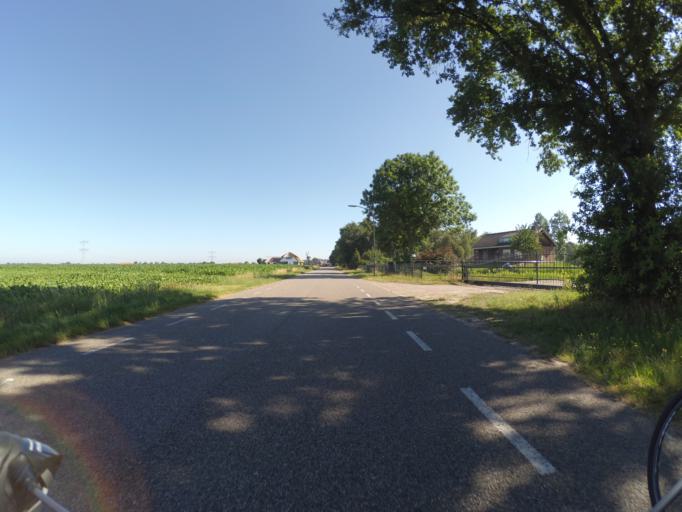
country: NL
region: North Brabant
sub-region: Gemeente Made en Drimmelen
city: Made
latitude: 51.6522
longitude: 4.8088
